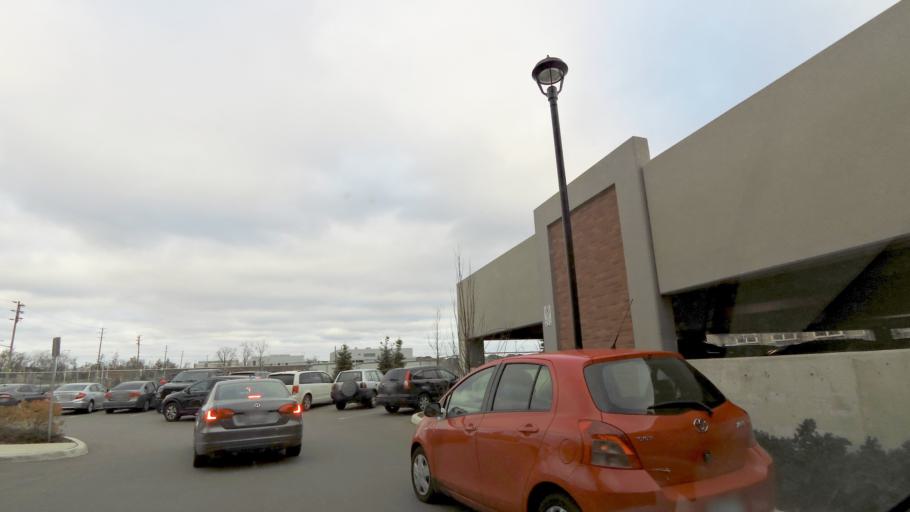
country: CA
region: Ontario
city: Burlington
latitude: 43.4359
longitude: -79.7752
